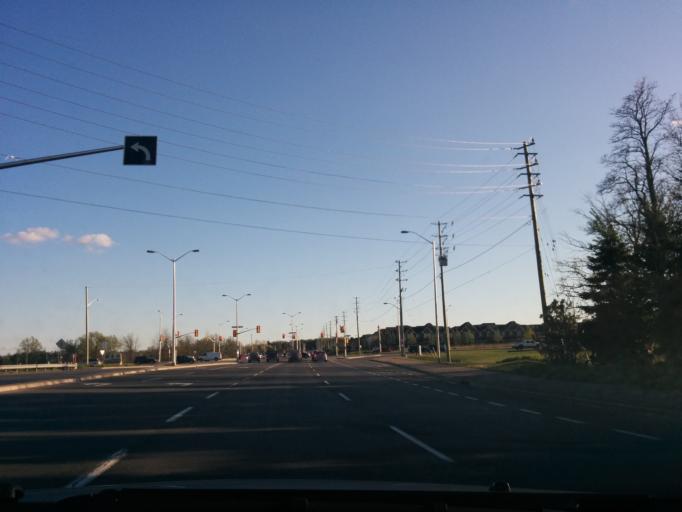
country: CA
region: Ontario
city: Bells Corners
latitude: 45.2722
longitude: -75.7044
